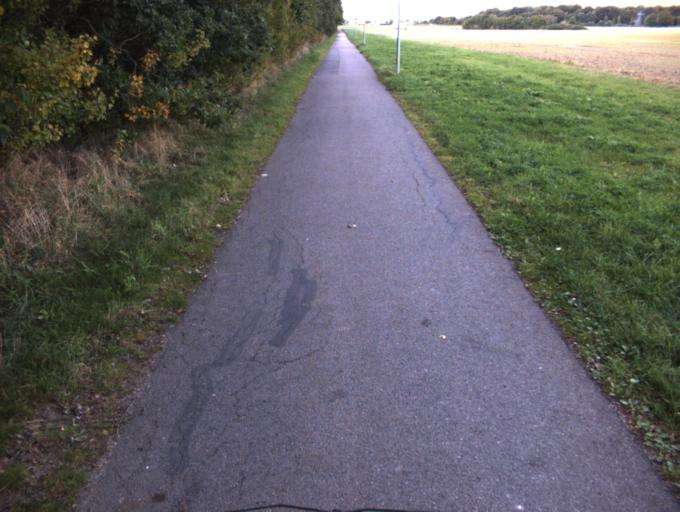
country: SE
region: Skane
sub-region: Helsingborg
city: Helsingborg
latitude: 56.0844
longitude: 12.6759
